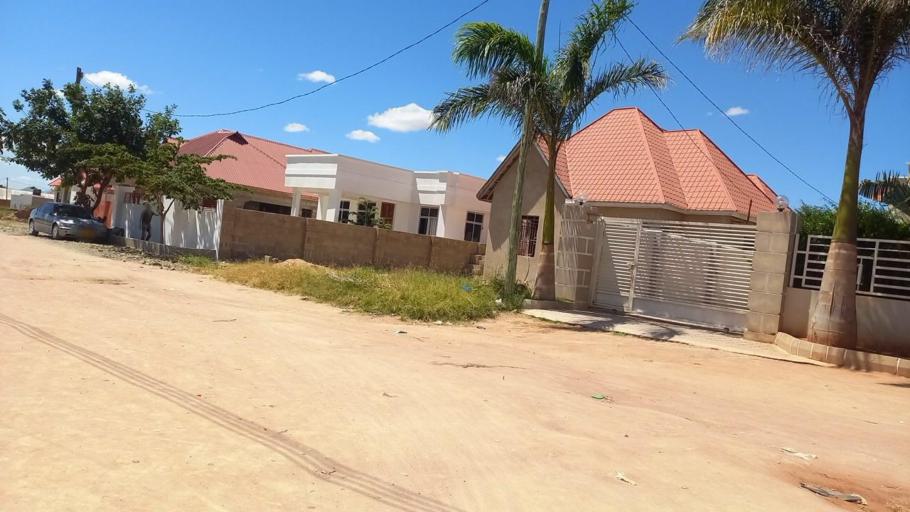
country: TZ
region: Dodoma
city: Dodoma
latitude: -6.1290
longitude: 35.7361
